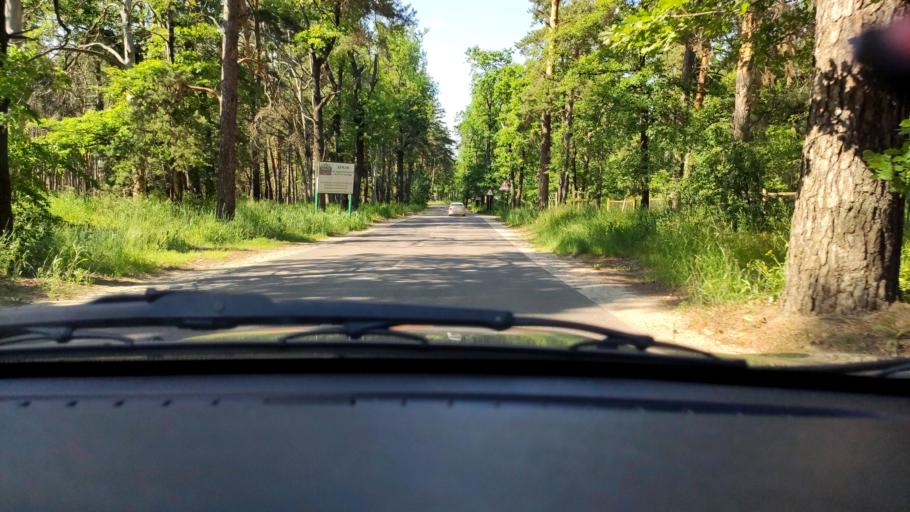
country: RU
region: Voronezj
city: Somovo
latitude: 51.7573
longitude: 39.3661
